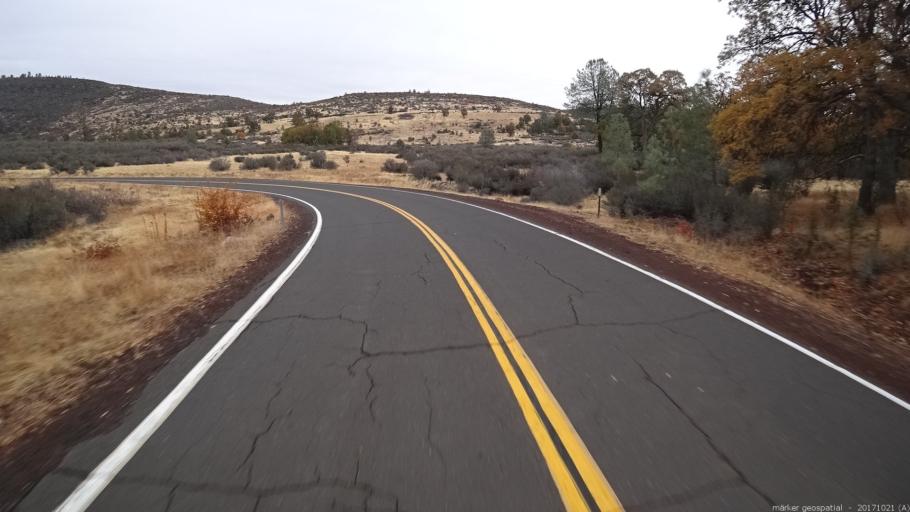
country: US
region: California
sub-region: Shasta County
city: Burney
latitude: 40.9978
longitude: -121.5033
